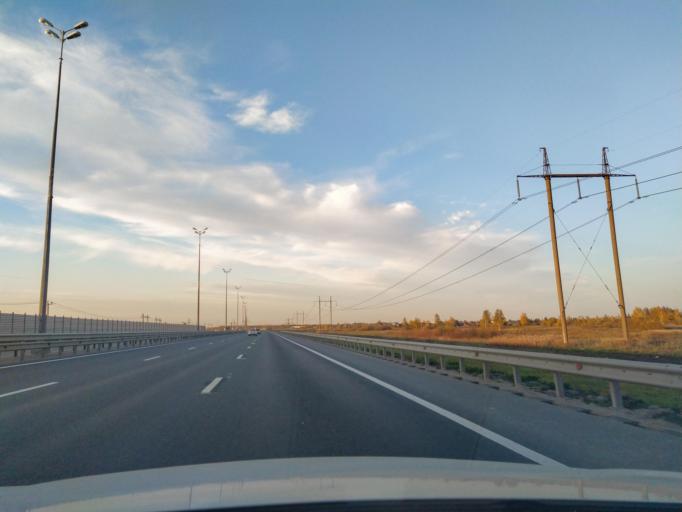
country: RU
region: Leningrad
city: Maloye Verevo
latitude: 59.5883
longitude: 30.1810
